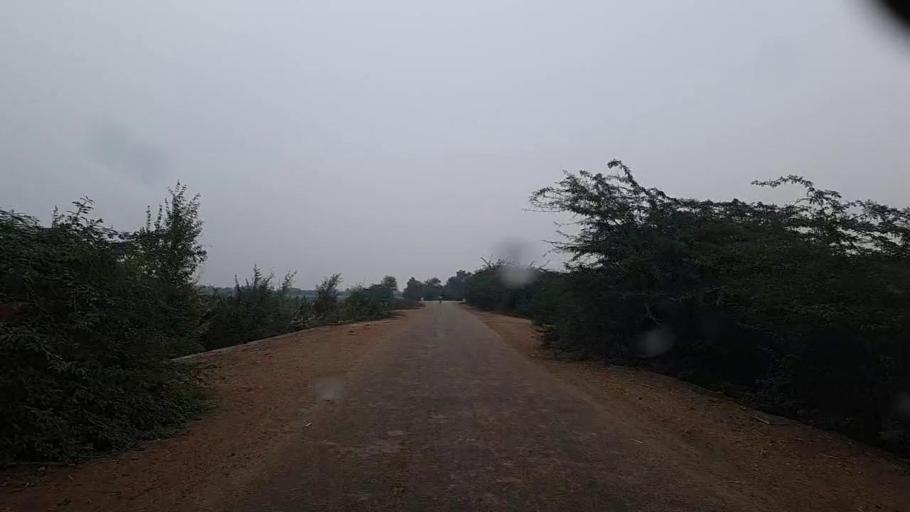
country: PK
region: Sindh
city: Ranipur
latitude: 27.2663
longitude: 68.5674
